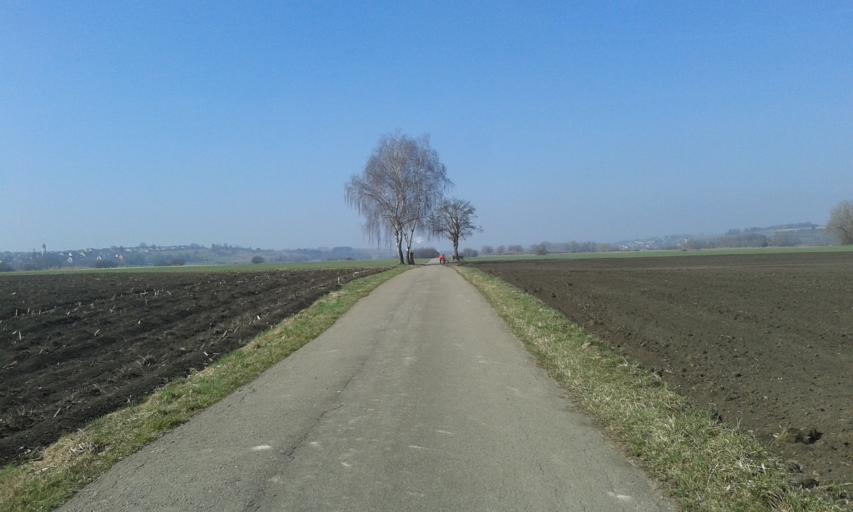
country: DE
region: Baden-Wuerttemberg
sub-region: Tuebingen Region
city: Opfingen
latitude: 48.2766
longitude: 9.8016
